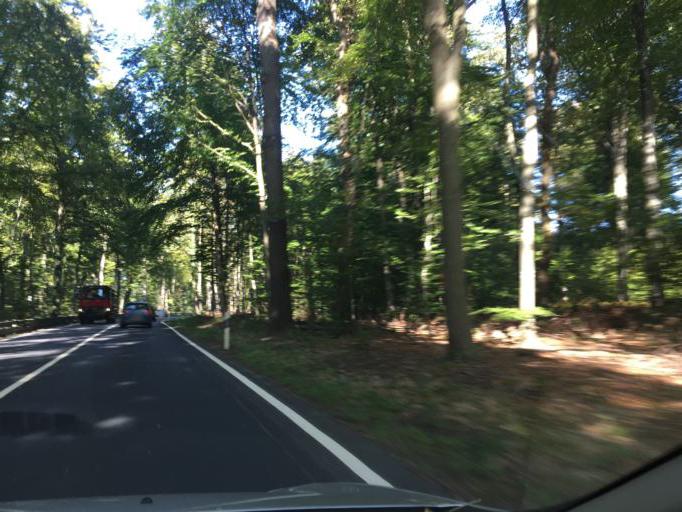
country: LU
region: Luxembourg
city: Bridel
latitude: 49.6447
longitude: 6.0678
